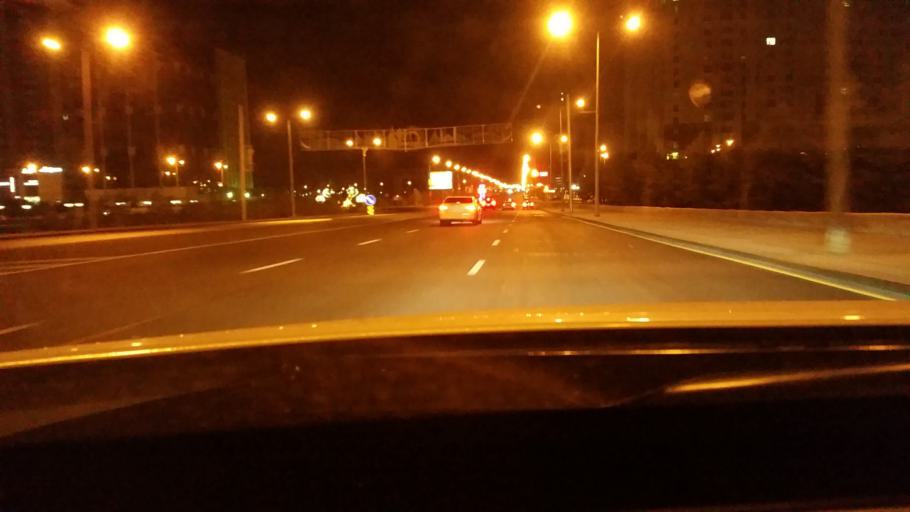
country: KZ
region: Astana Qalasy
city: Astana
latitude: 51.1298
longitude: 71.4556
